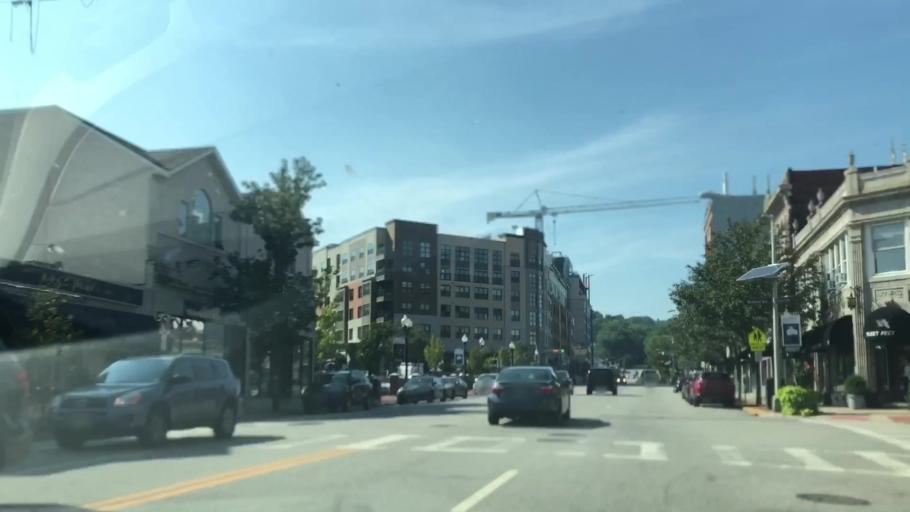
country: US
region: New Jersey
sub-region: Essex County
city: Montclair
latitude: 40.8158
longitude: -74.2201
